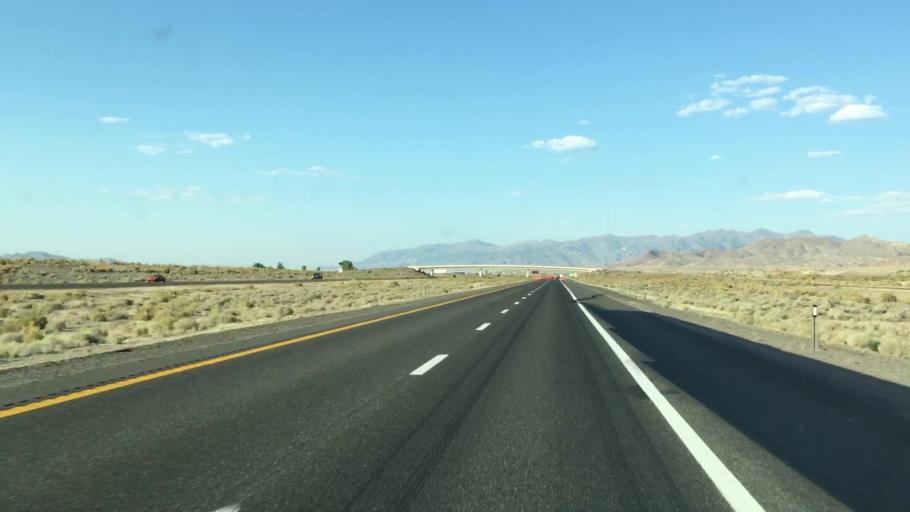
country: US
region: Nevada
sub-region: Pershing County
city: Lovelock
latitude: 40.2084
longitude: -118.4214
